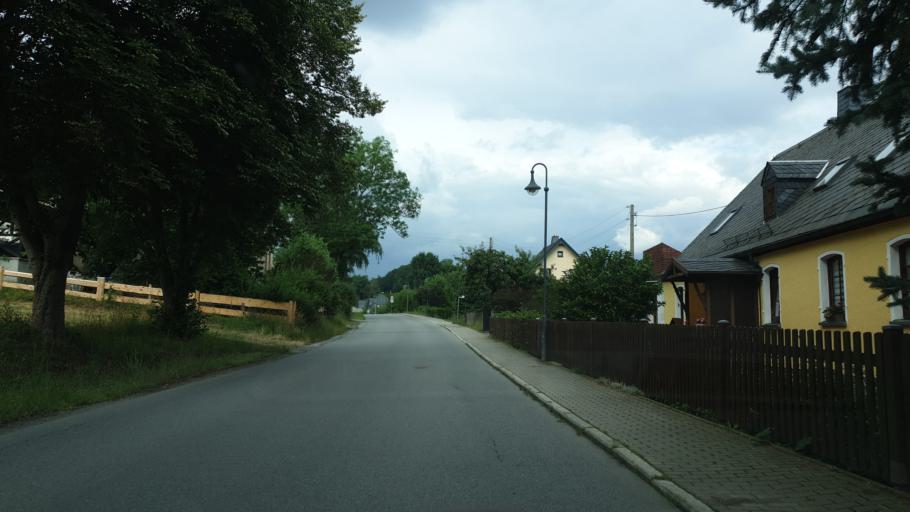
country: DE
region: Saxony
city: Lossnitz
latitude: 50.6404
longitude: 12.7534
